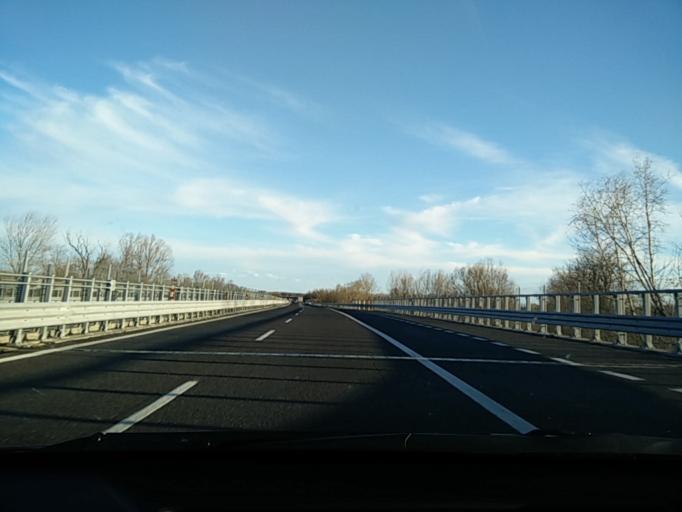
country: IT
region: Friuli Venezia Giulia
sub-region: Provincia di Udine
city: Buia
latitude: 46.2056
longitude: 13.0946
